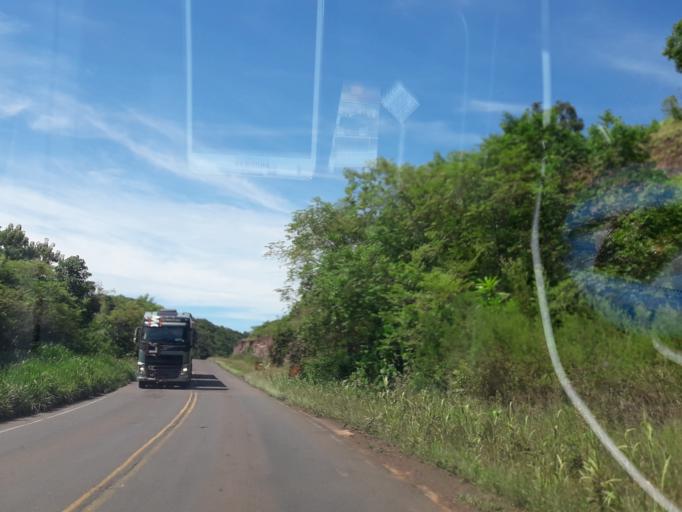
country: AR
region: Misiones
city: Bernardo de Irigoyen
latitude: -26.5160
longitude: -53.5165
